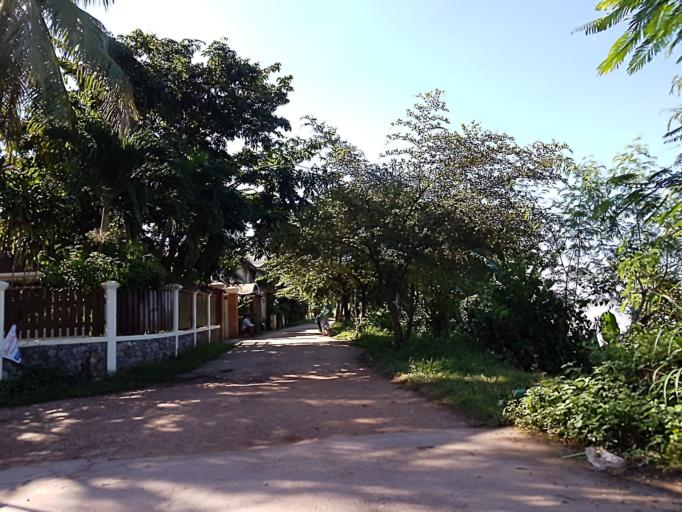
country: TH
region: Nong Khai
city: Si Chiang Mai
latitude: 17.9215
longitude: 102.6162
